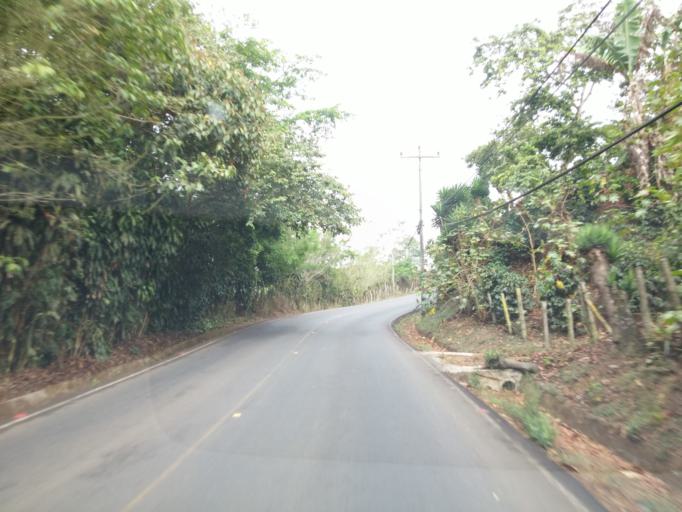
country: CR
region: Alajuela
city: San Ramon
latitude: 10.1380
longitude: -84.4761
